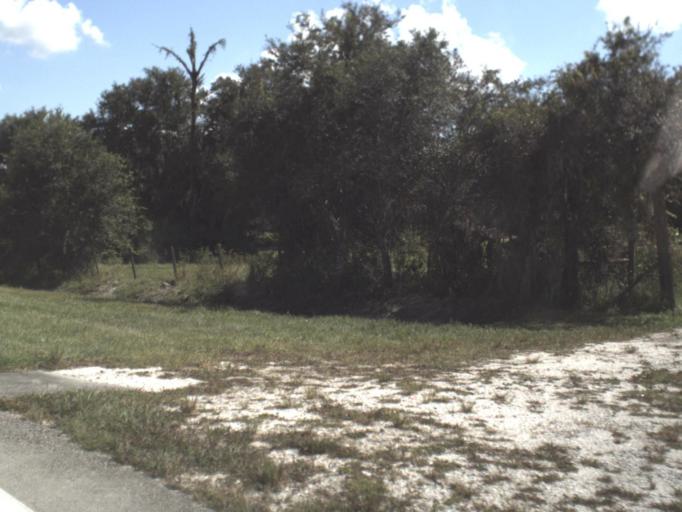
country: US
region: Florida
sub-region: Okeechobee County
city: Okeechobee
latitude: 27.3844
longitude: -80.9986
